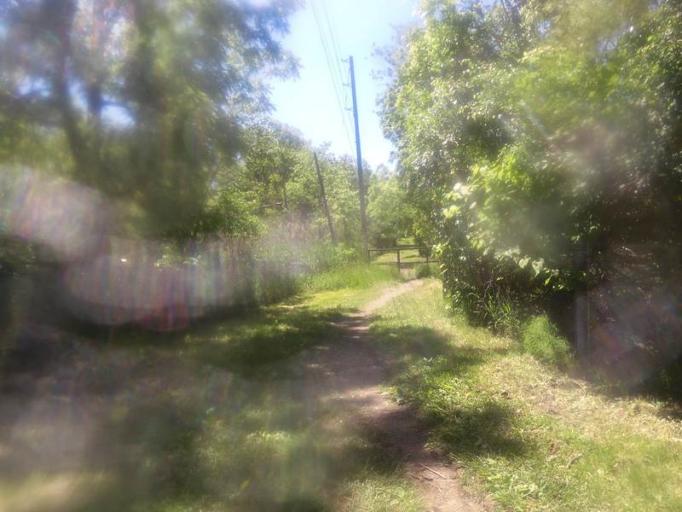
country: CA
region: Ontario
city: Kingston
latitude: 44.2445
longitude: -76.5361
